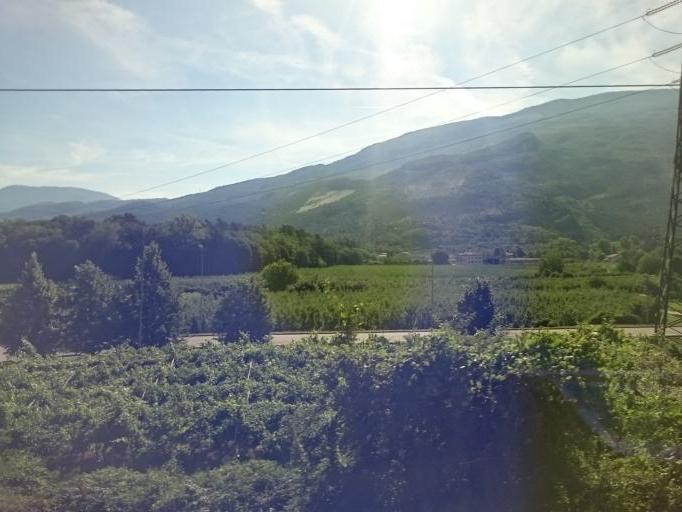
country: IT
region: Trentino-Alto Adige
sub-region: Provincia di Trento
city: Marco
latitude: 45.8483
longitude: 11.0025
